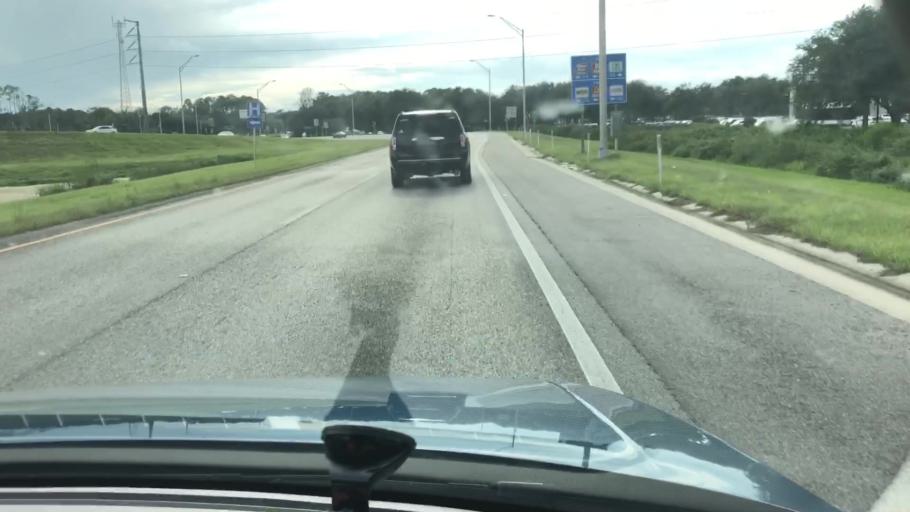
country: US
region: Florida
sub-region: Seminole County
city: Lake Mary
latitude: 28.8139
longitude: -81.3383
